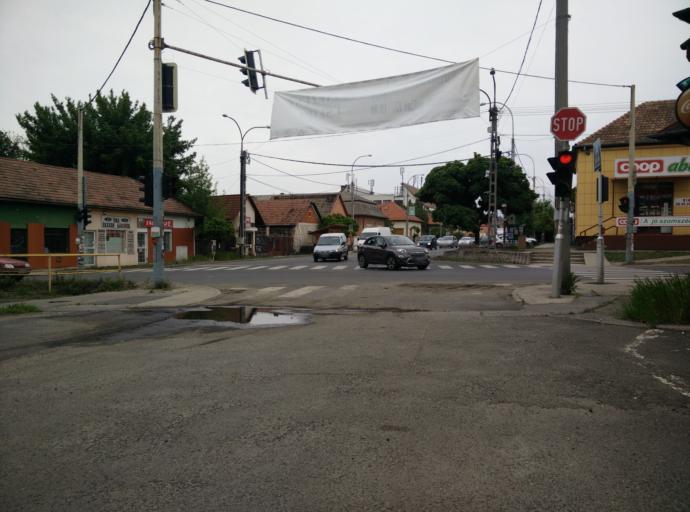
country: HU
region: Pest
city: Fot
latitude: 47.6091
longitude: 19.1929
